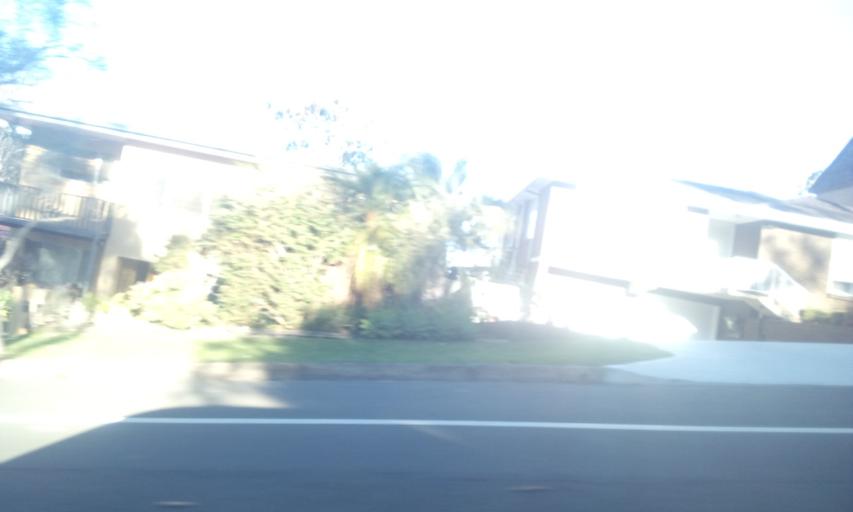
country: AU
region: New South Wales
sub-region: Wollongong
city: Mount Keira
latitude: -34.4250
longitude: 150.8466
